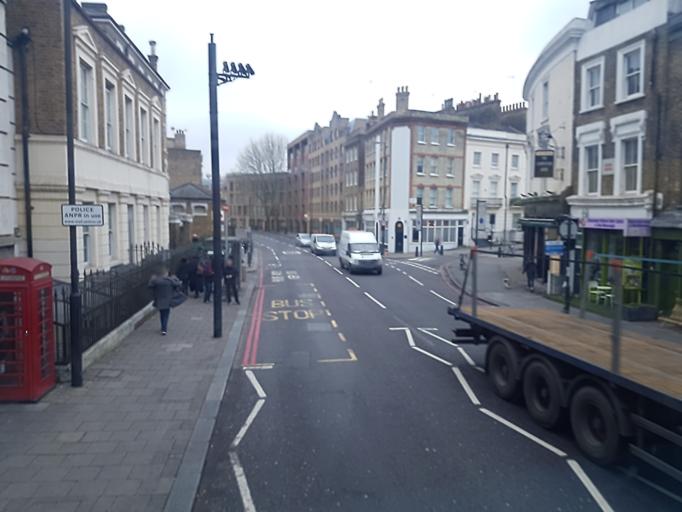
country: GB
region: England
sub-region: Greater London
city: Clerkenwell
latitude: 51.5288
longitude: -0.1157
